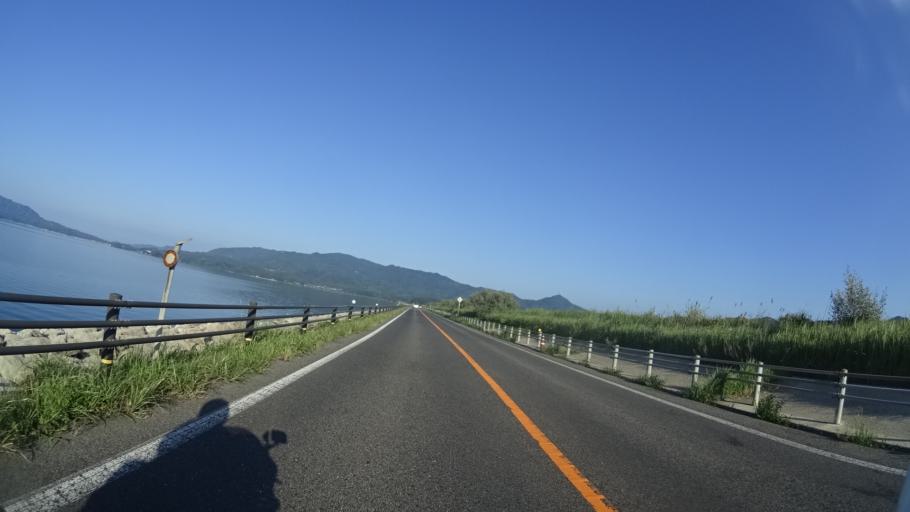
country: JP
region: Shimane
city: Sakaiminato
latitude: 35.5242
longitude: 133.1799
